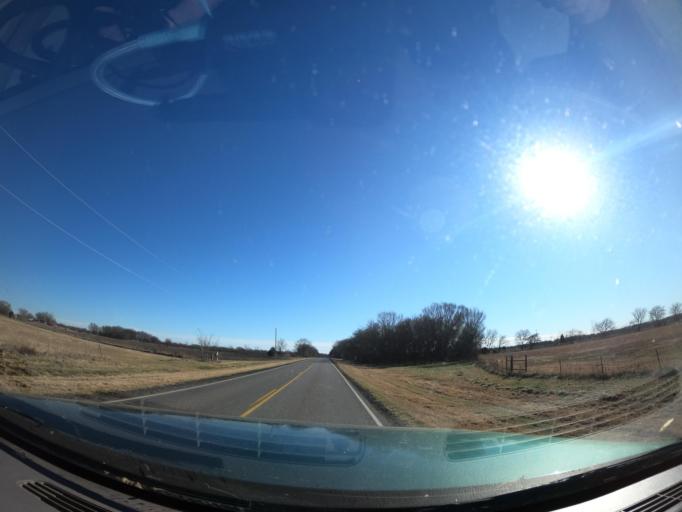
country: US
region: Oklahoma
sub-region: McIntosh County
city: Checotah
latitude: 35.5677
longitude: -95.6554
